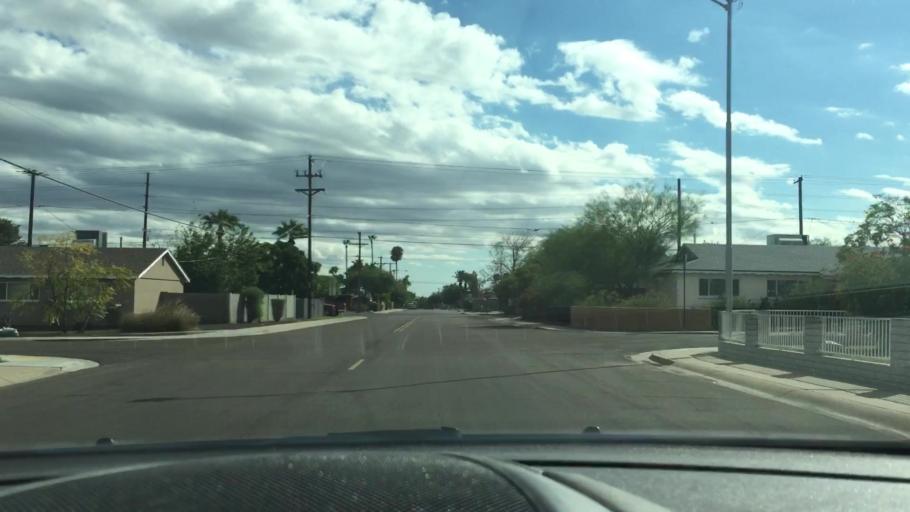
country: US
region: Arizona
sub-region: Maricopa County
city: Tempe
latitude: 33.4523
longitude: -111.9222
